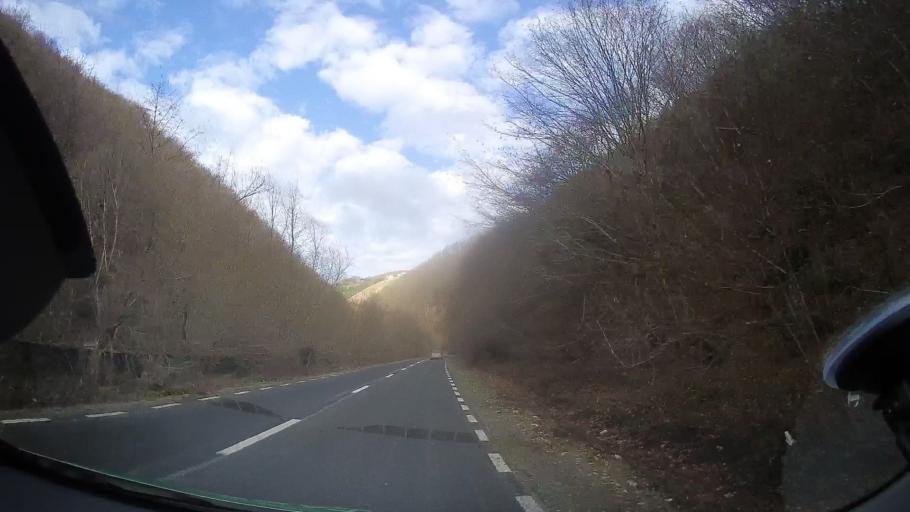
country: RO
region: Cluj
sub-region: Comuna Baisoara
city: Baisoara
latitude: 46.5886
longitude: 23.4418
